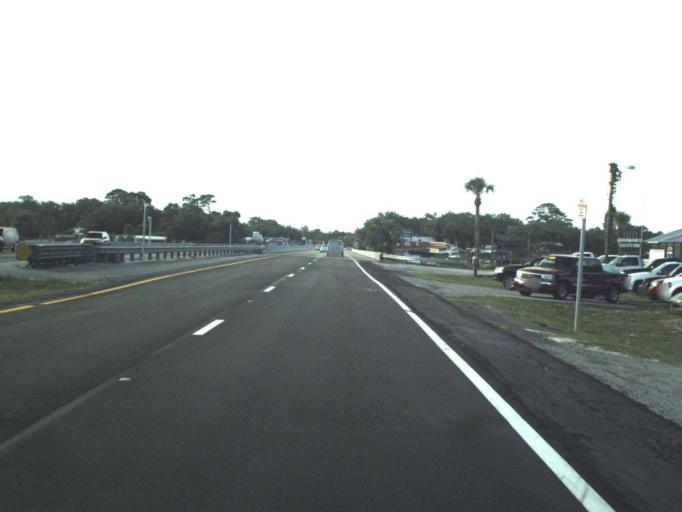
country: US
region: Florida
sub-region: Volusia County
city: Ponce Inlet
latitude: 29.1018
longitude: -80.9710
